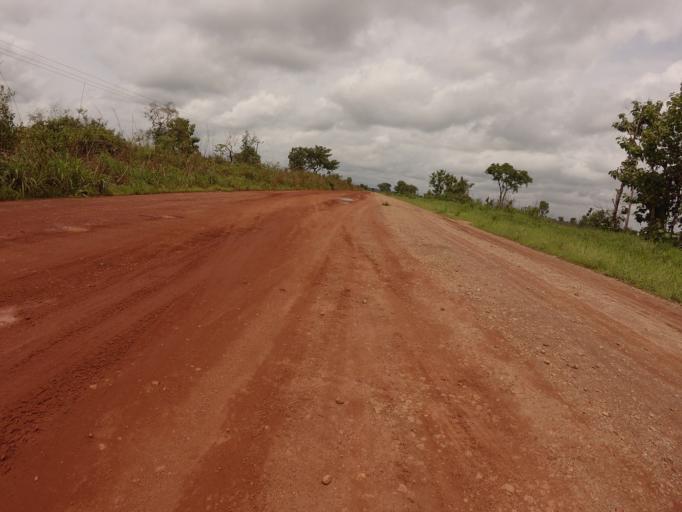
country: GH
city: Kpandae
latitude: 8.4494
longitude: 0.3501
